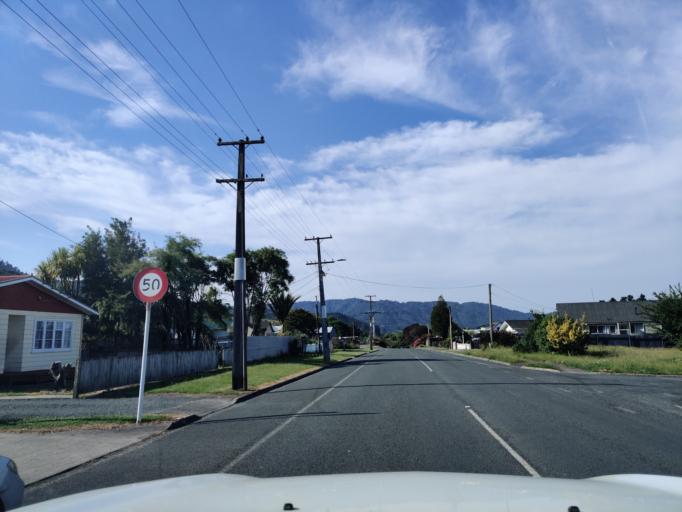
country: NZ
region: Waikato
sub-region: Waikato District
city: Ngaruawahia
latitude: -37.6627
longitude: 175.1432
